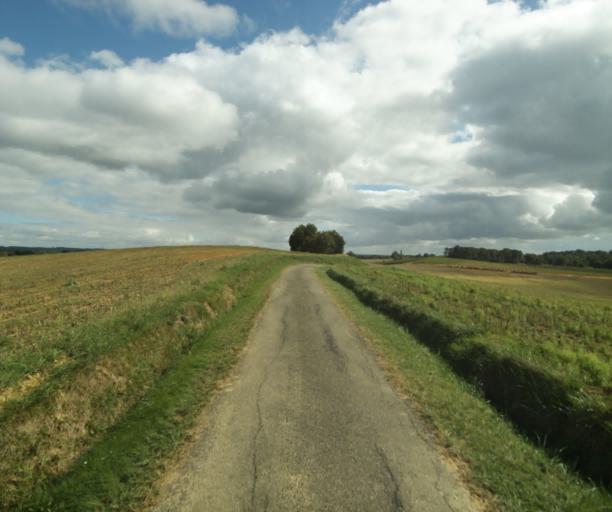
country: FR
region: Midi-Pyrenees
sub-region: Departement du Gers
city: Cazaubon
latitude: 43.8506
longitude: -0.0378
